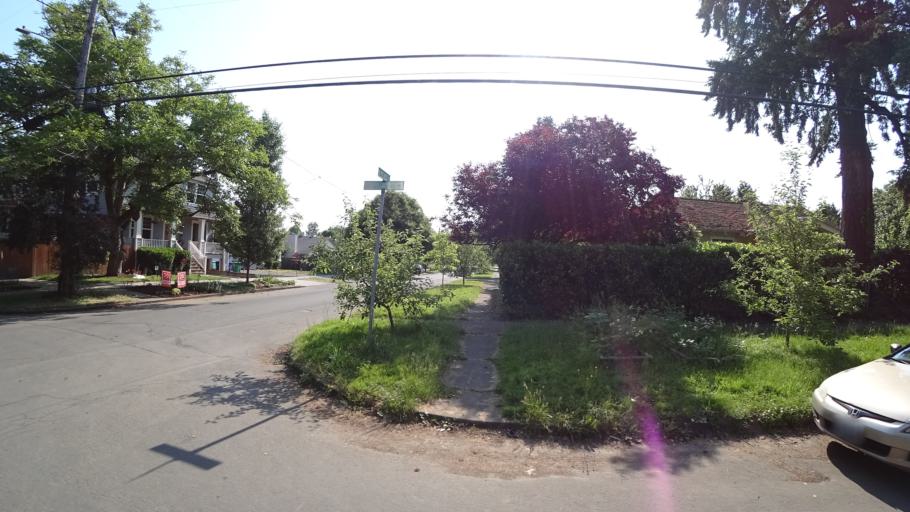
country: US
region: Washington
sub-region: Clark County
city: Vancouver
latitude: 45.5945
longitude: -122.7325
